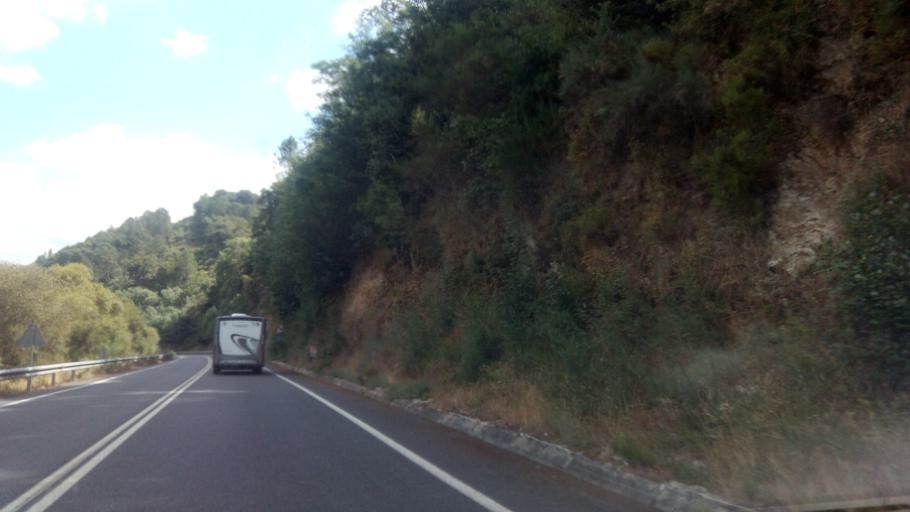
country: ES
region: Galicia
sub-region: Provincia de Ourense
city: Nogueira de Ramuin
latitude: 42.4199
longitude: -7.7693
